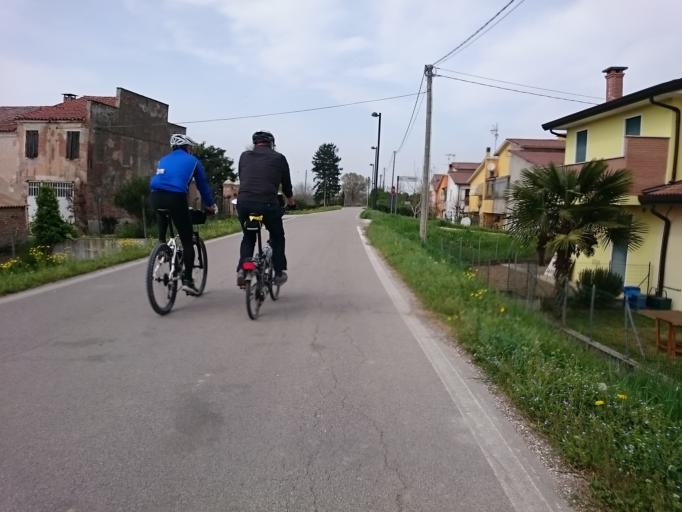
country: IT
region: Veneto
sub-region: Provincia di Padova
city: Bagnoli di Sopra
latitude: 45.1670
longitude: 11.8491
